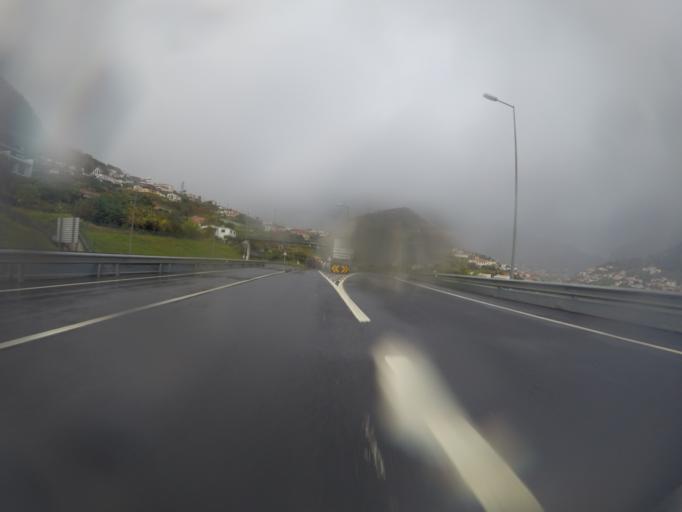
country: PT
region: Madeira
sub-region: Machico
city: Machico
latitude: 32.7268
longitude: -16.7785
